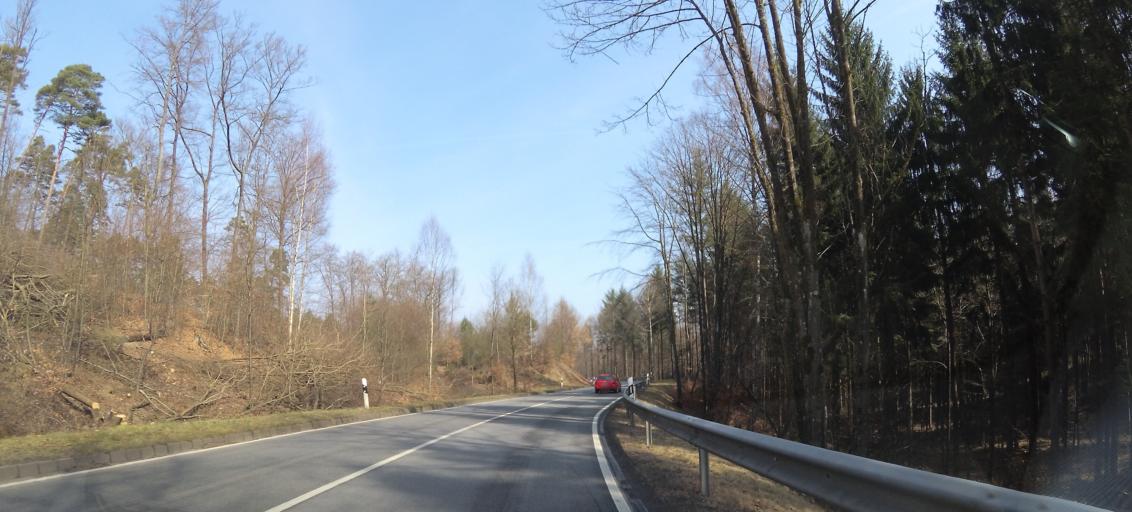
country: DE
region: Rheinland-Pfalz
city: Stelzenberg
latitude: 49.4137
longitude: 7.7475
